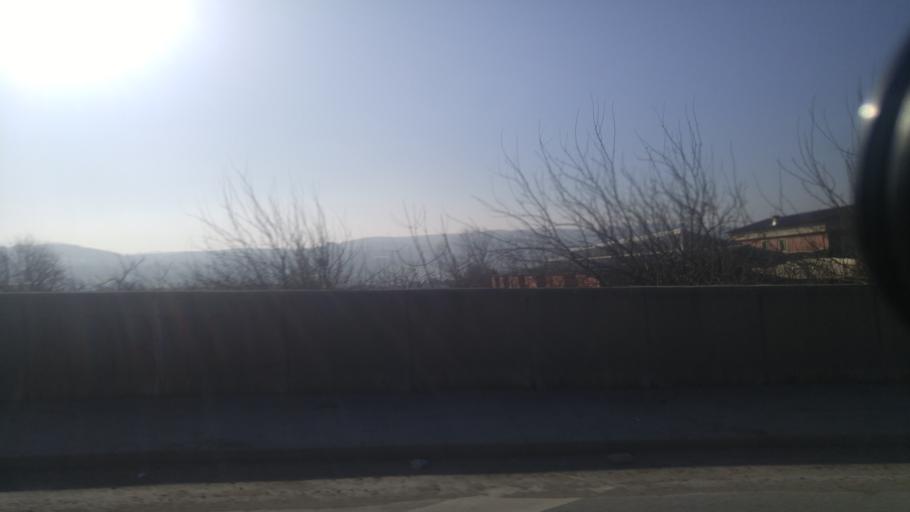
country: TR
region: Istanbul
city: Muratbey
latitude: 41.0899
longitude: 28.5140
